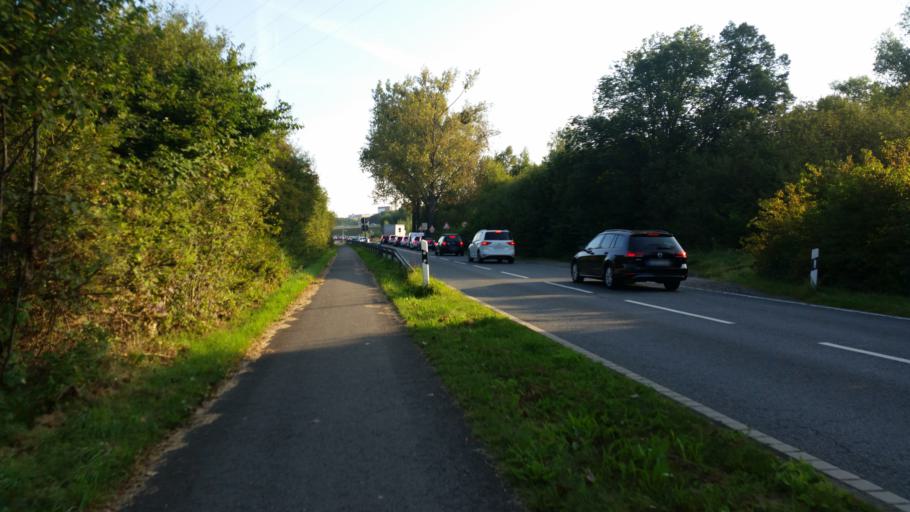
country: DE
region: Lower Saxony
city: Weyhausen
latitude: 52.4292
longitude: 10.7346
